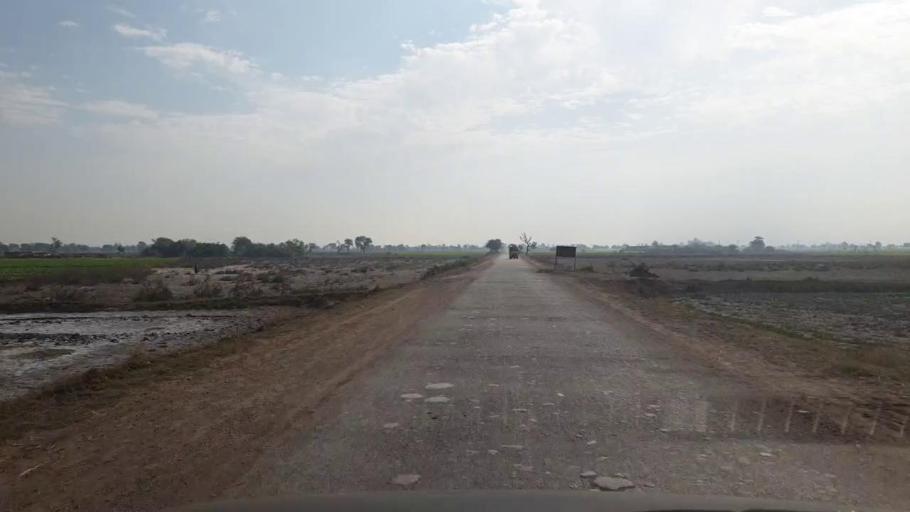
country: PK
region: Sindh
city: Hala
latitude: 25.9991
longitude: 68.4088
